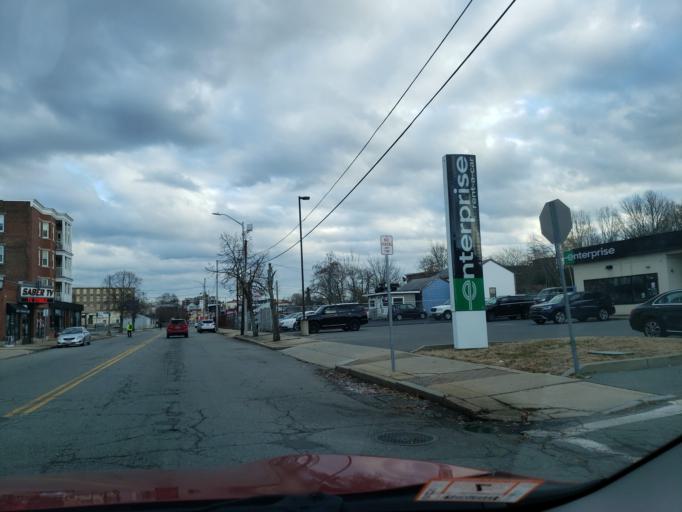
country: US
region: Massachusetts
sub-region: Bristol County
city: Fall River
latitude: 41.6968
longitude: -71.1426
